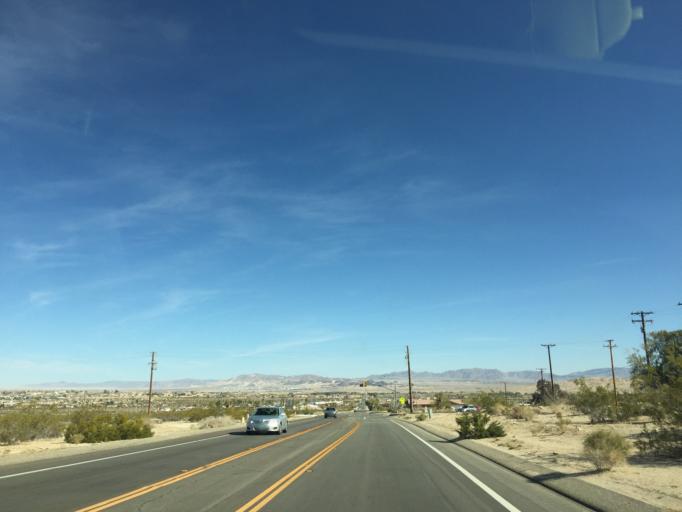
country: US
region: California
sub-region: San Bernardino County
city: Twentynine Palms
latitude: 34.1199
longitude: -116.0366
